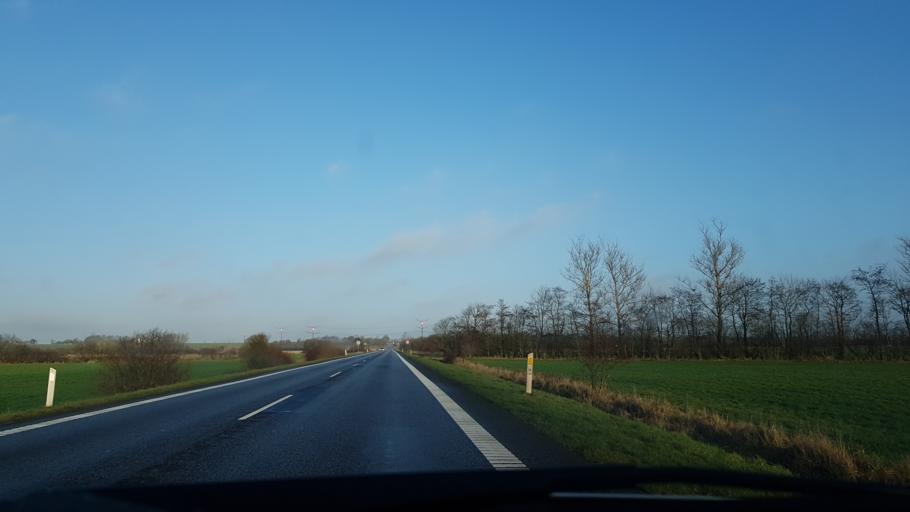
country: DK
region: South Denmark
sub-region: Tonder Kommune
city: Toftlund
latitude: 55.2412
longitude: 9.1311
